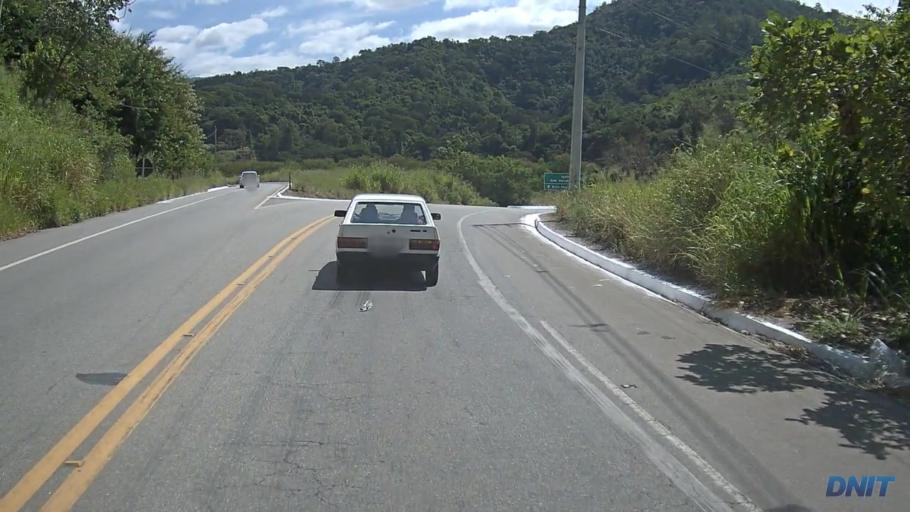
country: BR
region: Minas Gerais
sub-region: Timoteo
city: Timoteo
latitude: -19.5421
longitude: -42.6857
